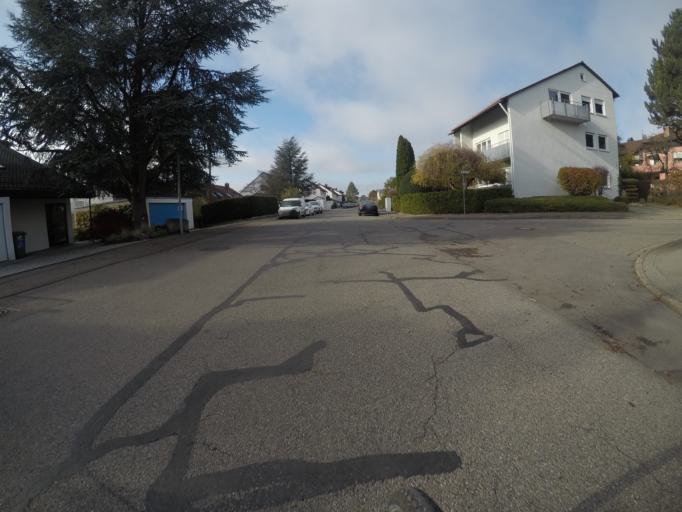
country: DE
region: Baden-Wuerttemberg
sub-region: Regierungsbezirk Stuttgart
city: Leinfelden-Echterdingen
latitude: 48.7183
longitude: 9.1512
